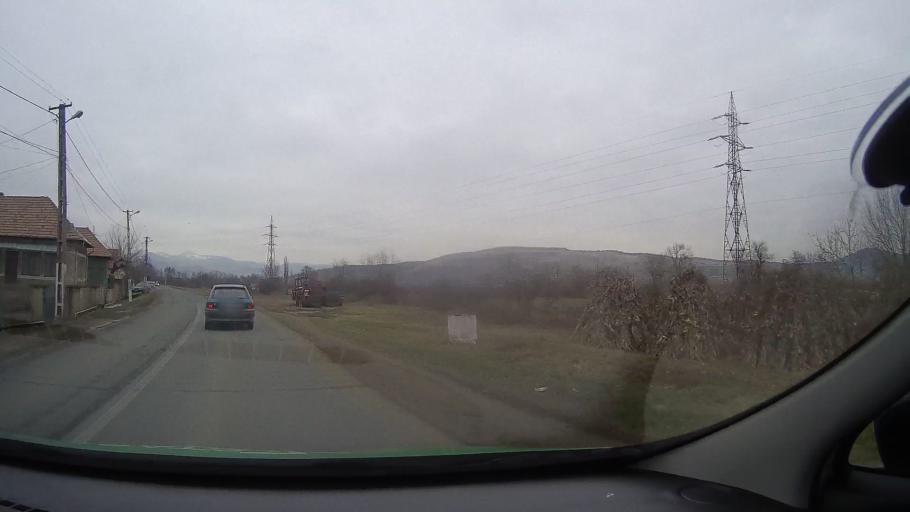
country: RO
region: Alba
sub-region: Comuna Ighiu
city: Sard
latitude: 46.1185
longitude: 23.5364
